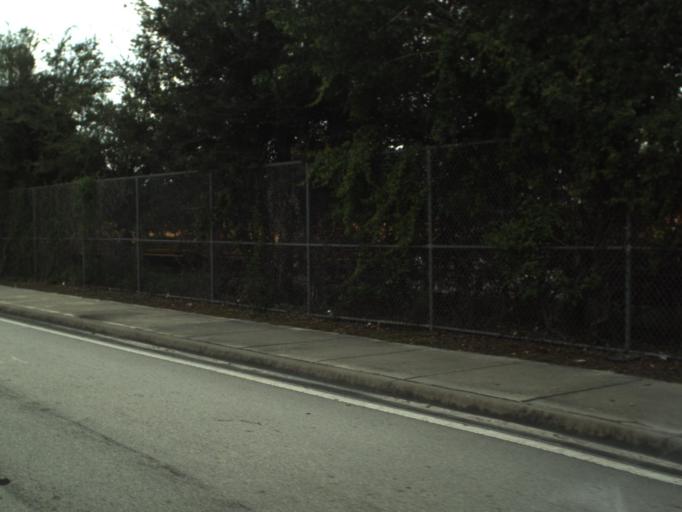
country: US
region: Florida
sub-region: Miami-Dade County
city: Tamiami
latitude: 25.7741
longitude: -80.4174
